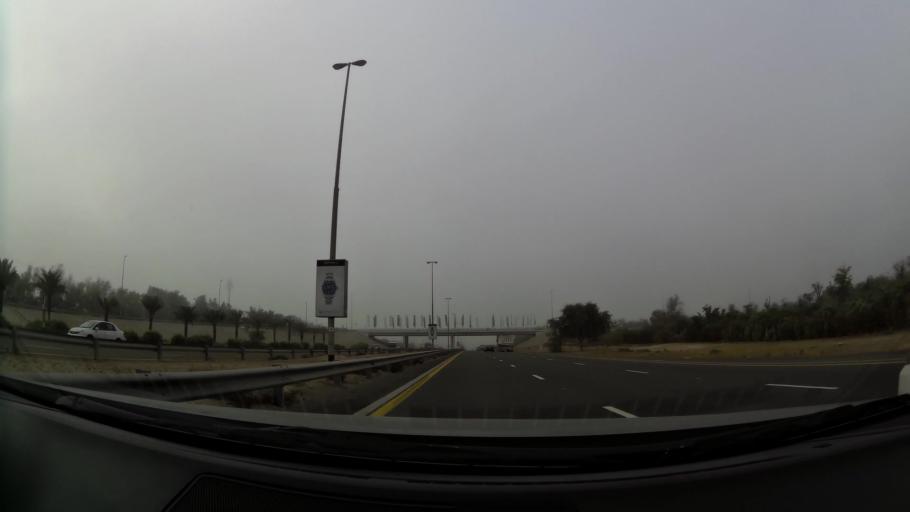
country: AE
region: Dubai
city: Dubai
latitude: 25.1522
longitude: 55.3384
